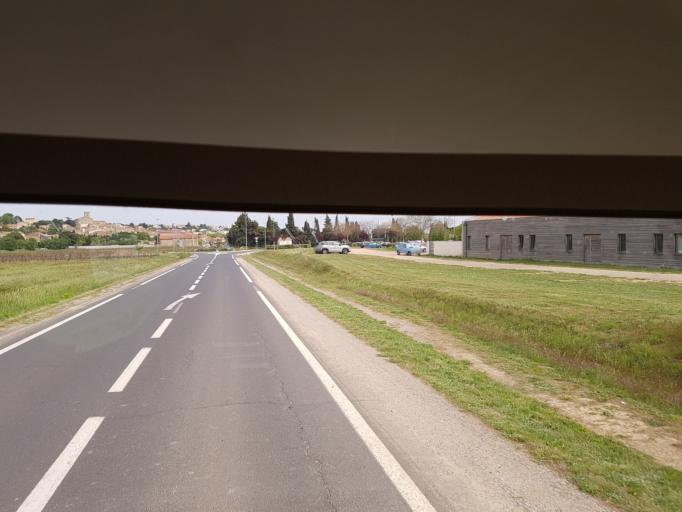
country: FR
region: Languedoc-Roussillon
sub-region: Departement de l'Herault
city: Vendres
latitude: 43.2705
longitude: 3.2154
